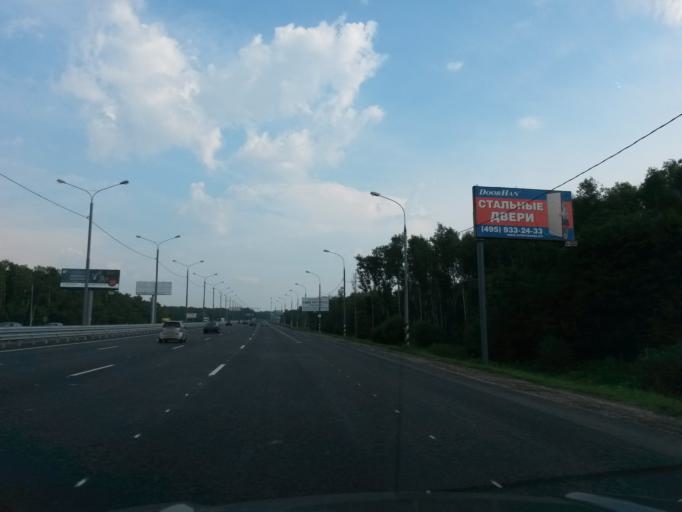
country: RU
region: Moscow
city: Annino
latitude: 55.5391
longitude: 37.6095
